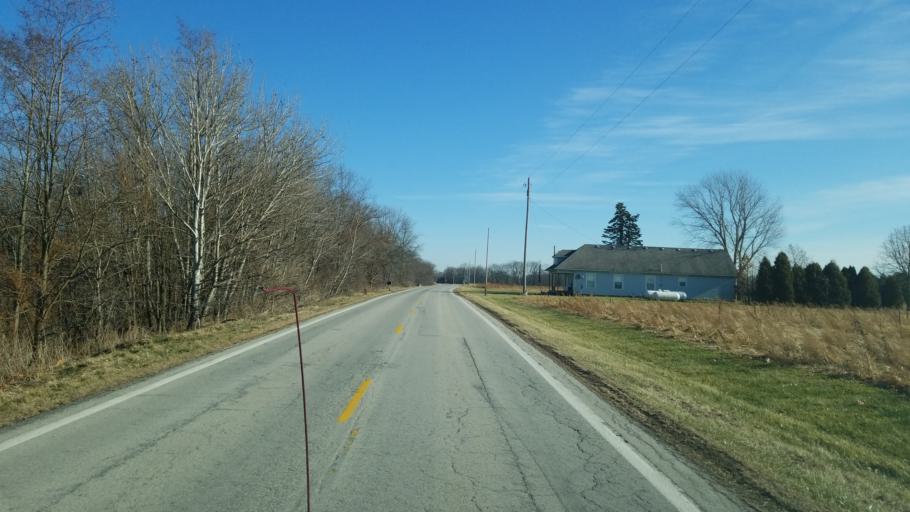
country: US
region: Ohio
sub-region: Henry County
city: Liberty Center
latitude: 41.4151
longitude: -83.9461
